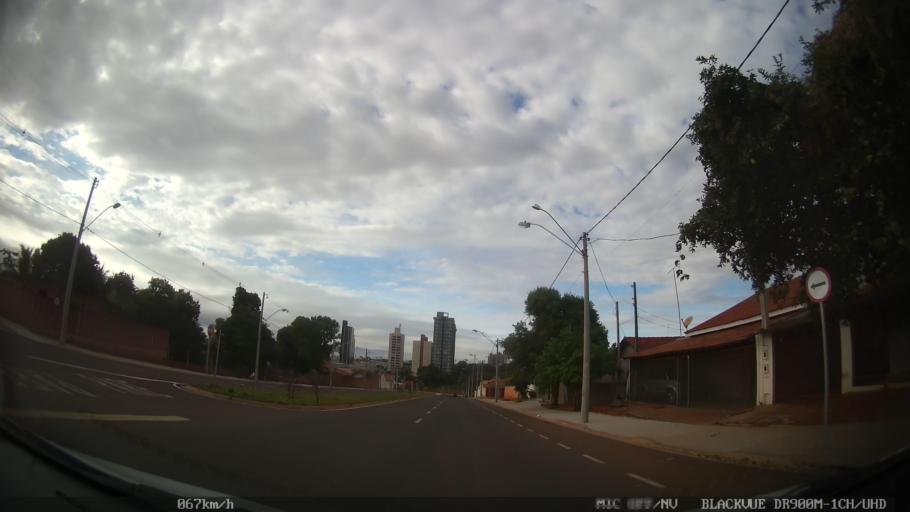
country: BR
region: Sao Paulo
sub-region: Sao Jose Do Rio Preto
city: Sao Jose do Rio Preto
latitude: -20.8291
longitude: -49.4113
